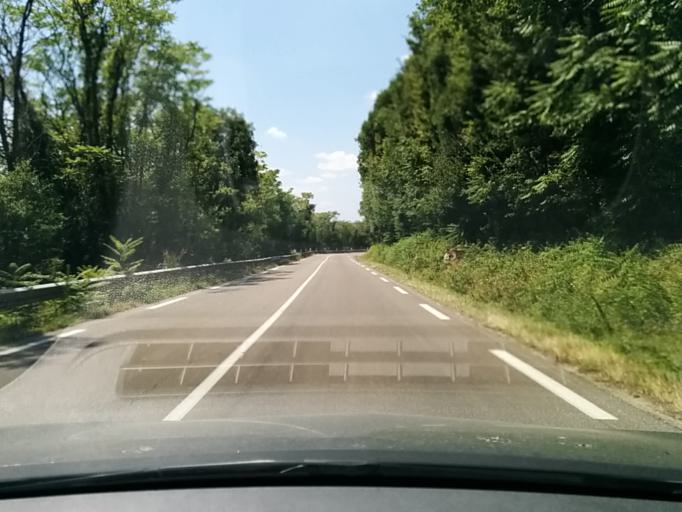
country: FR
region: Midi-Pyrenees
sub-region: Departement du Gers
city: Vic-Fezensac
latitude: 43.7496
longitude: 0.3294
